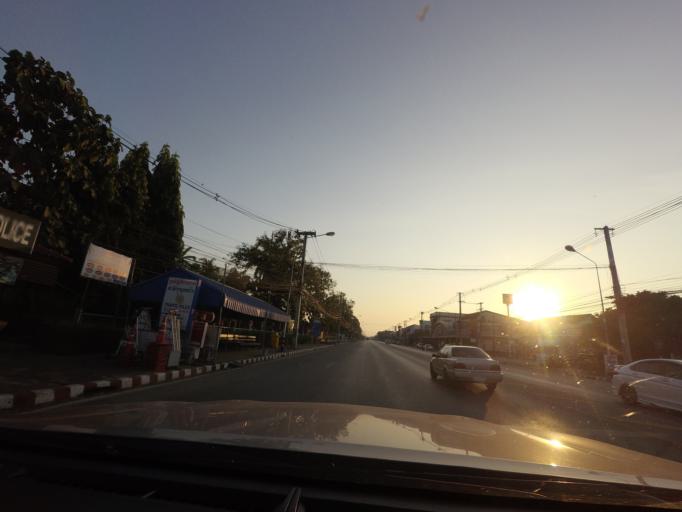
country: TH
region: Sukhothai
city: Si Samrong
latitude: 17.1624
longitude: 99.8615
